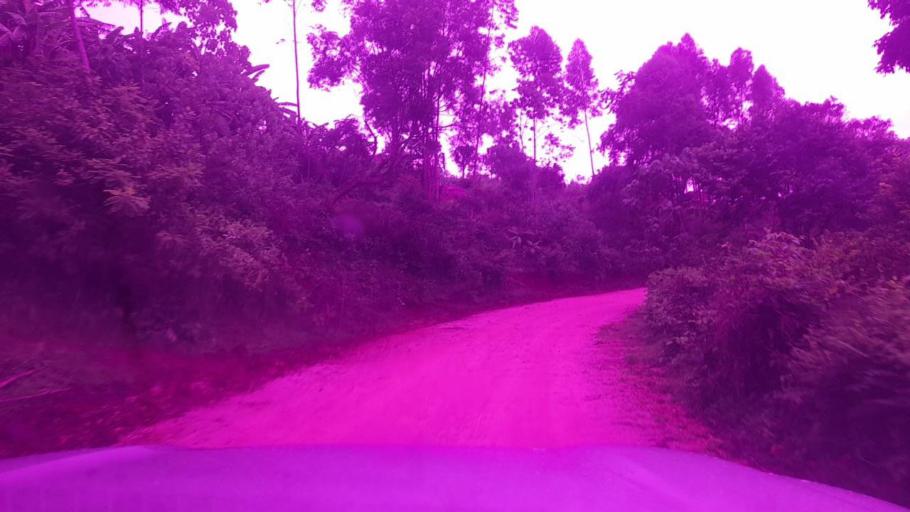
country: ET
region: Southern Nations, Nationalities, and People's Region
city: Bonga
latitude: 7.4515
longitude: 36.1293
